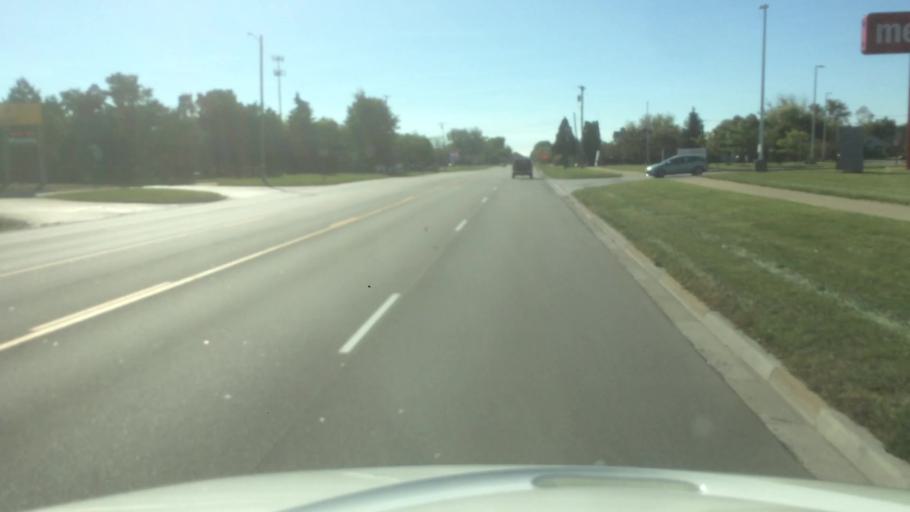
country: US
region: Michigan
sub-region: Macomb County
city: Fraser
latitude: 42.5522
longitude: -82.9606
